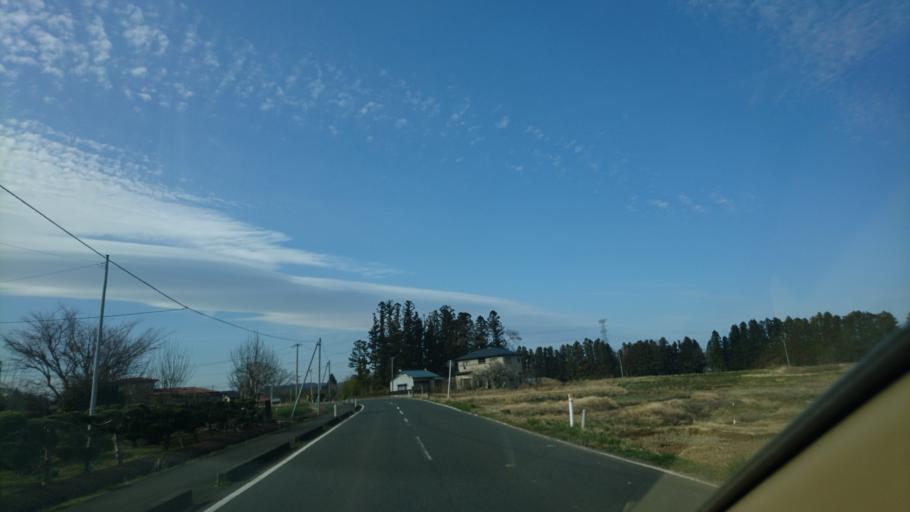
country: JP
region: Iwate
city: Ichinoseki
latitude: 38.8087
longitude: 141.0312
